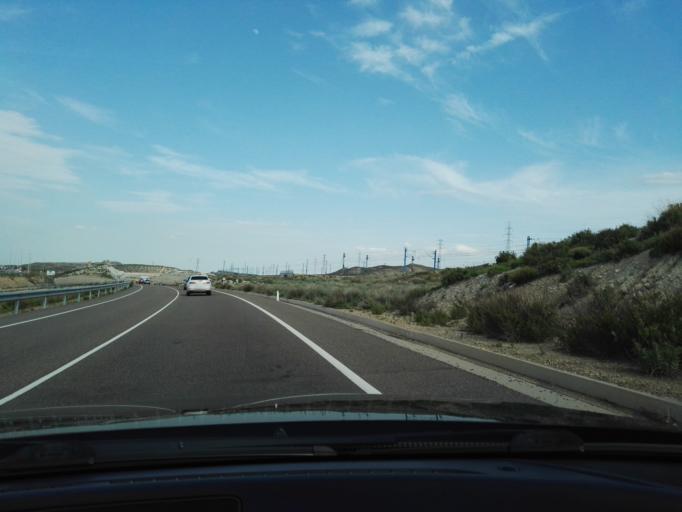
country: ES
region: Aragon
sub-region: Provincia de Zaragoza
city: Montecanal
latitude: 41.6188
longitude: -0.9681
